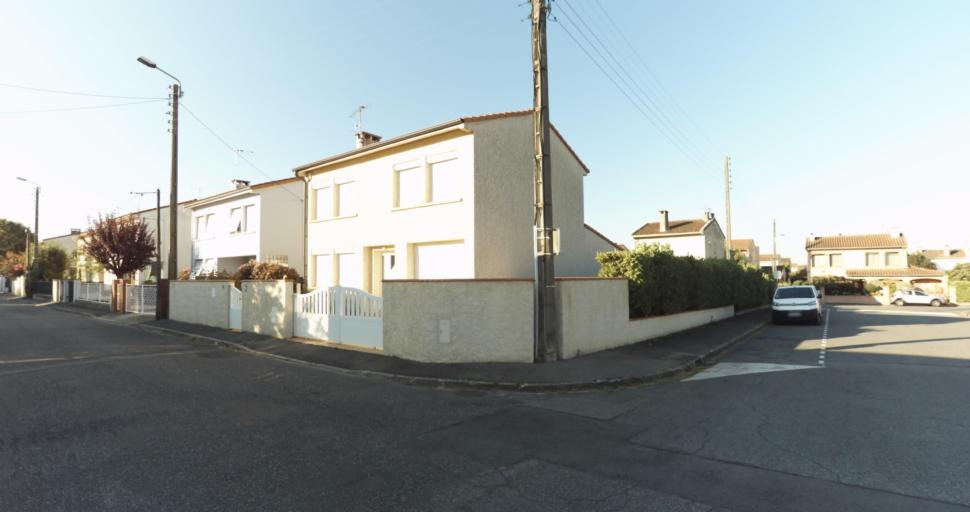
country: FR
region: Midi-Pyrenees
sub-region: Departement de la Haute-Garonne
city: L'Union
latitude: 43.6579
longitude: 1.4729
